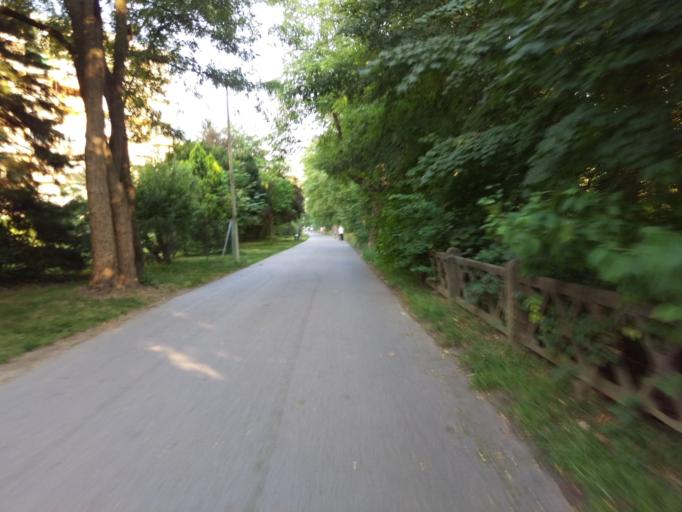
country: AT
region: Styria
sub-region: Graz Stadt
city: Graz
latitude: 47.0836
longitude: 15.4273
